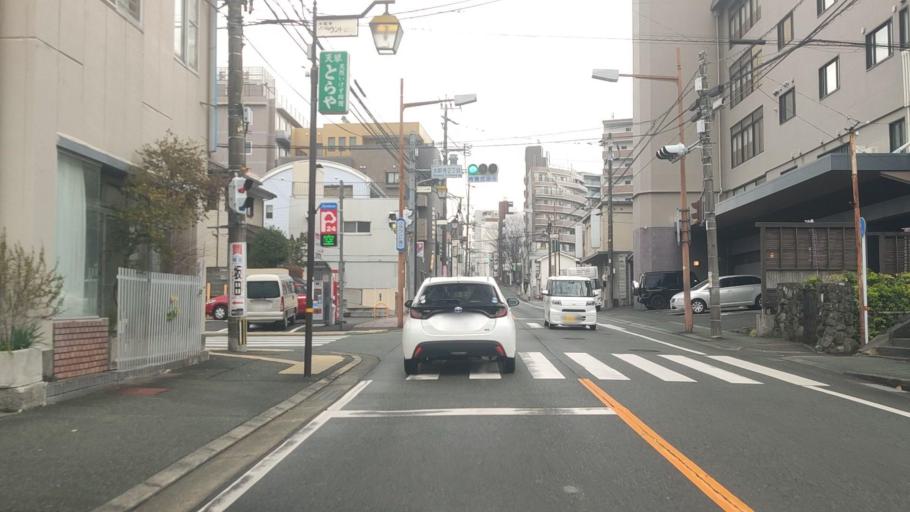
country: JP
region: Kumamoto
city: Kumamoto
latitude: 32.7925
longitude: 130.7360
